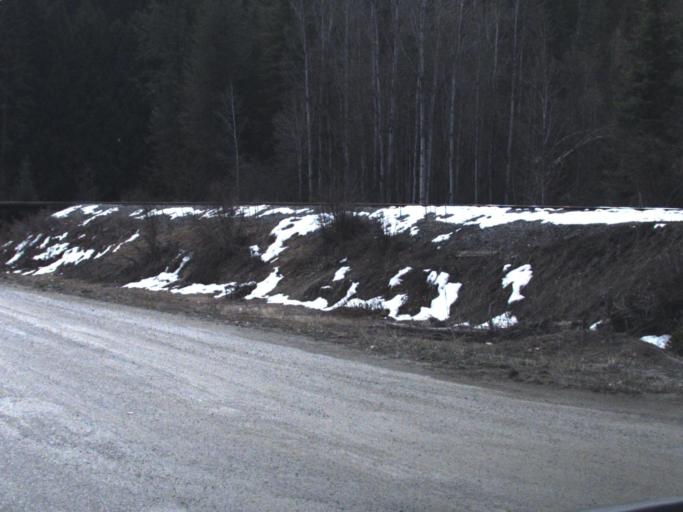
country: US
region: Washington
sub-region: Stevens County
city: Chewelah
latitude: 48.5551
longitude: -117.3452
